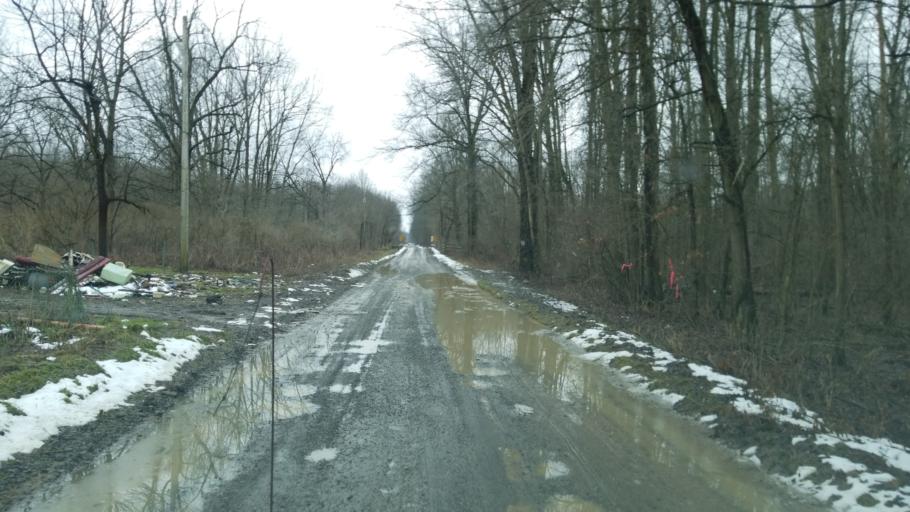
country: US
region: Ohio
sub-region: Ashtabula County
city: Orwell
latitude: 41.4368
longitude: -80.9349
